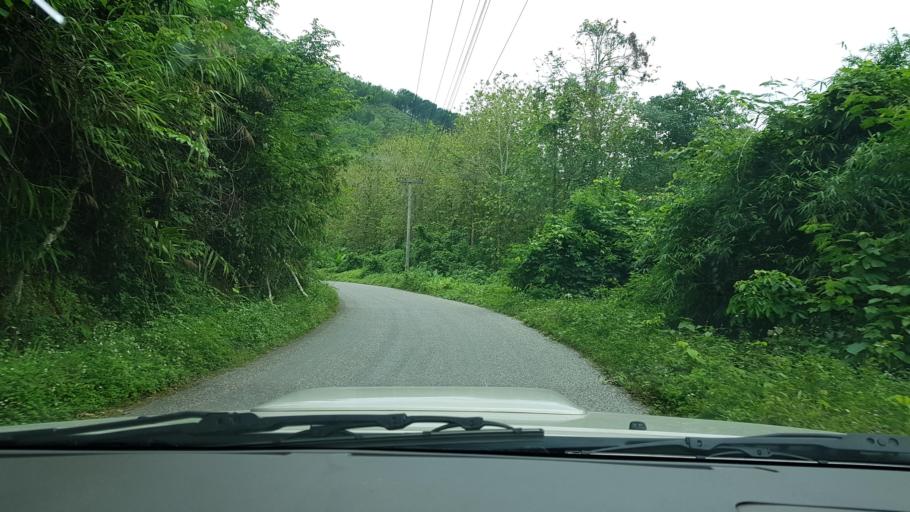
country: LA
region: Phongsali
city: Khoa
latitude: 21.0606
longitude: 102.3851
